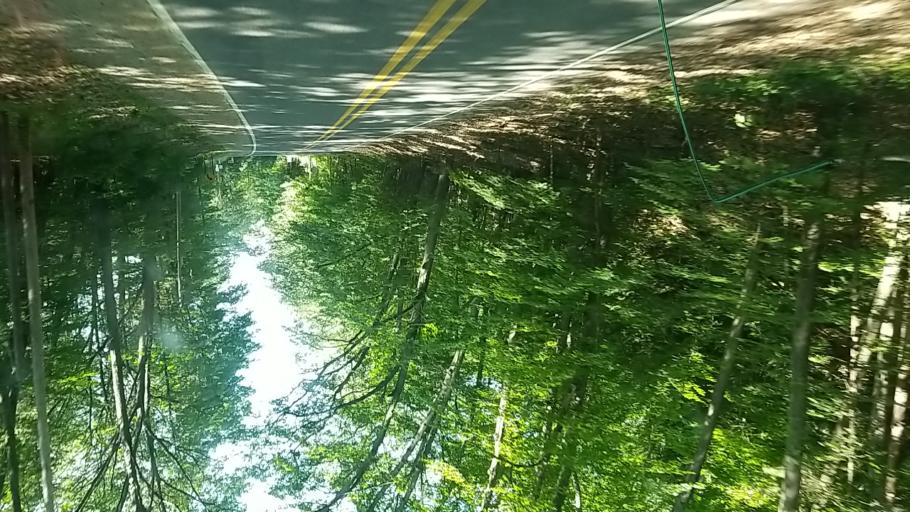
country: US
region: Michigan
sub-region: Muskegon County
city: Whitehall
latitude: 43.3345
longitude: -86.4003
